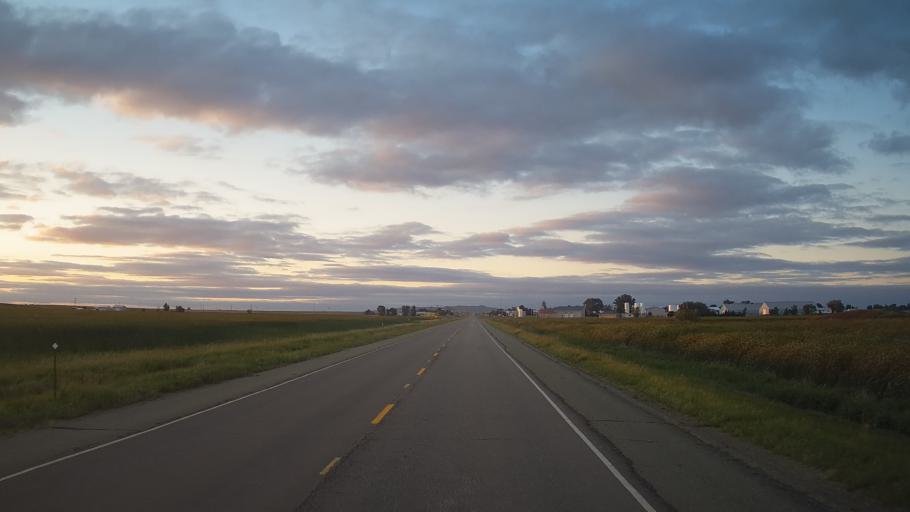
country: US
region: South Dakota
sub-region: Lyman County
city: Kennebec
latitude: 43.8706
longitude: -99.6061
